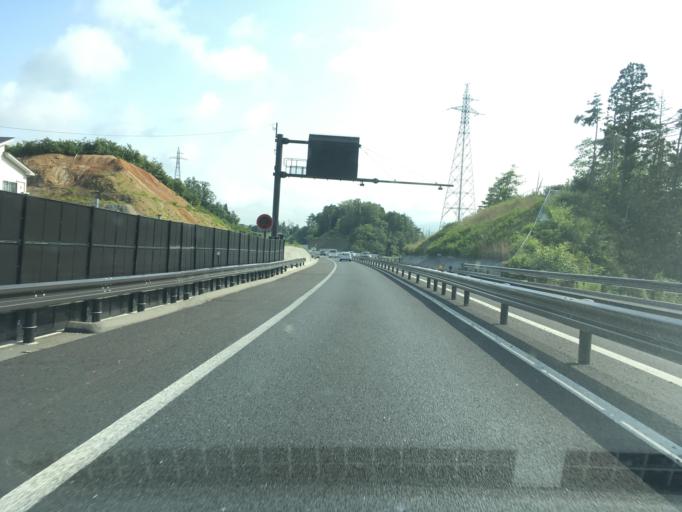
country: JP
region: Iwate
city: Ofunato
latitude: 38.9178
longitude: 141.5921
